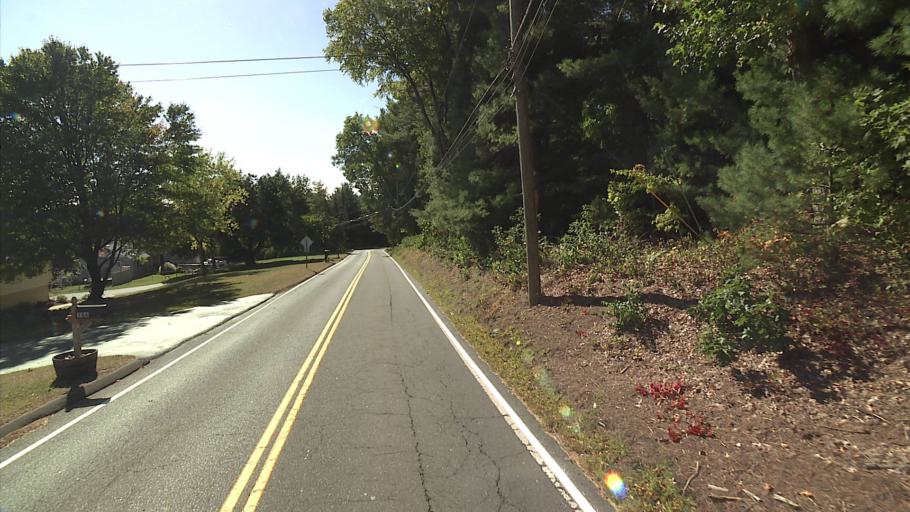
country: US
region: Connecticut
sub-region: Hartford County
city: Bristol
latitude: 41.7277
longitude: -72.9503
